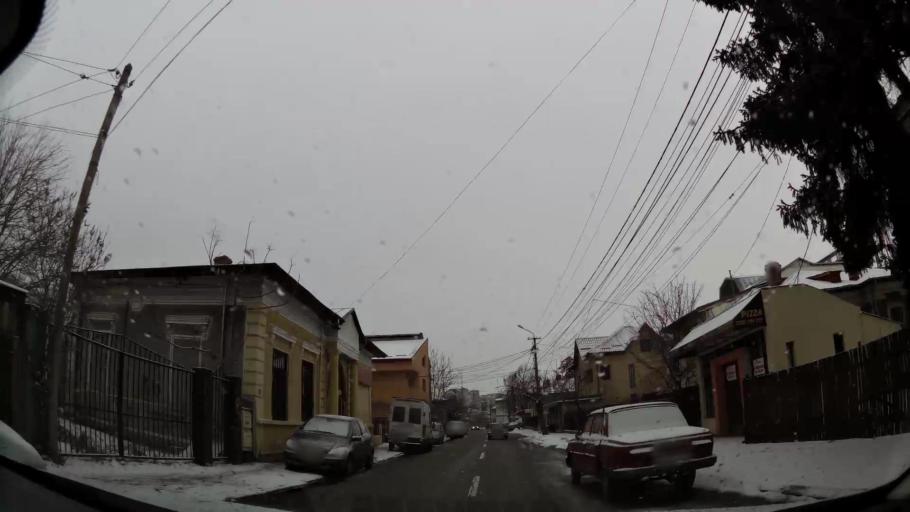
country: RO
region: Dambovita
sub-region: Municipiul Targoviste
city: Targoviste
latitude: 44.9289
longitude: 25.4548
